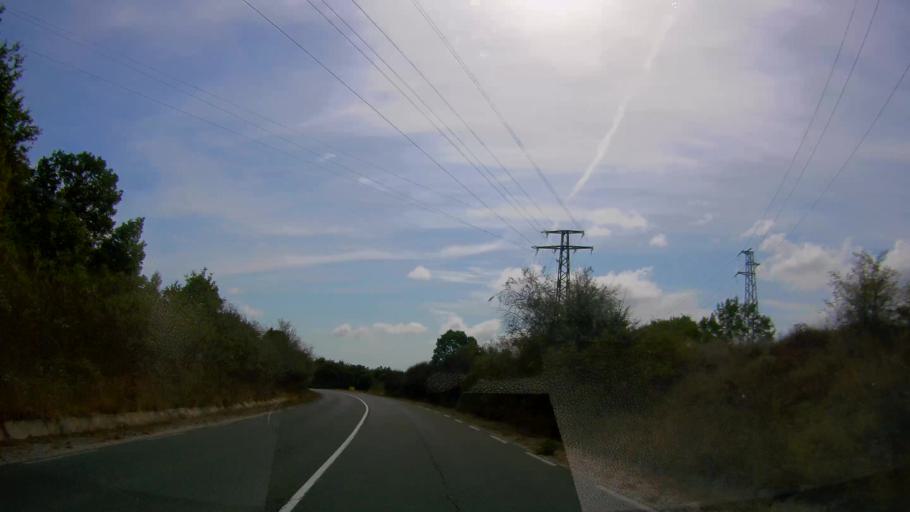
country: BG
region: Burgas
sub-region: Obshtina Sozopol
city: Sozopol
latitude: 42.3693
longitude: 27.6845
